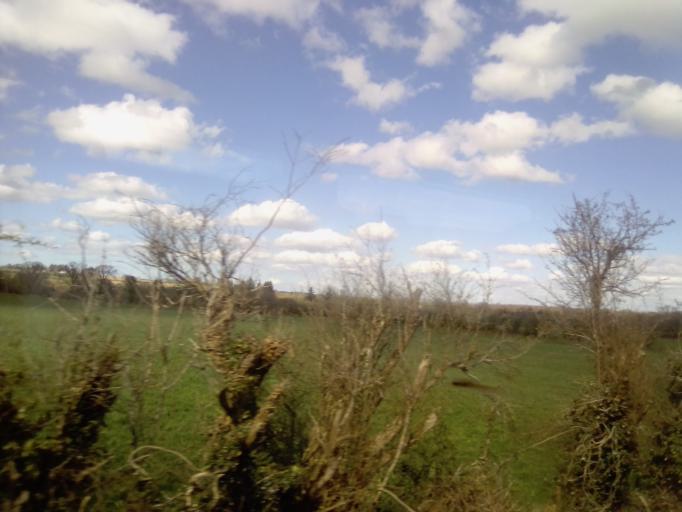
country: IE
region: Munster
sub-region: County Cork
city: Kanturk
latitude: 52.1284
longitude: -8.8883
